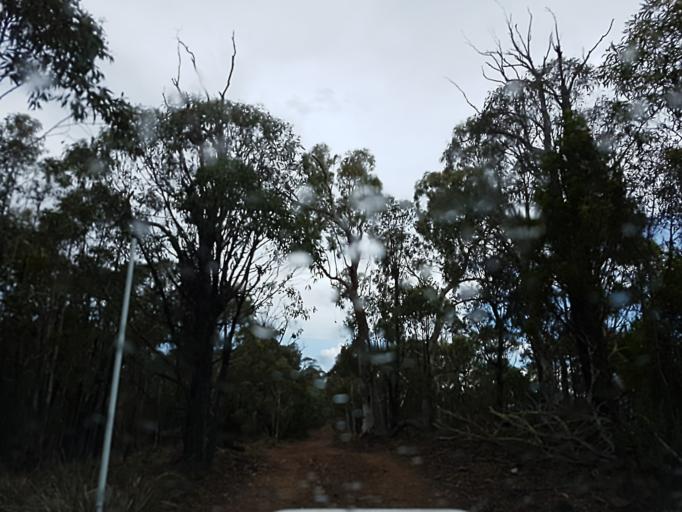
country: AU
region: New South Wales
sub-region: Snowy River
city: Jindabyne
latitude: -36.9035
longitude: 148.3424
